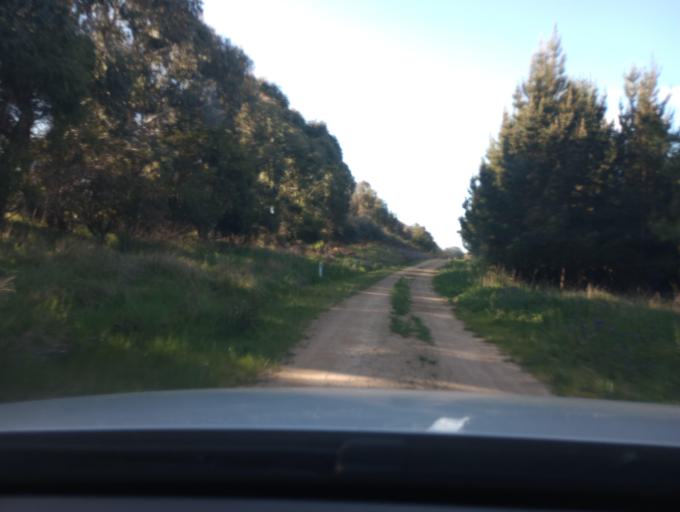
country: AU
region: New South Wales
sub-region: Blayney
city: Millthorpe
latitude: -33.4024
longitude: 149.3084
